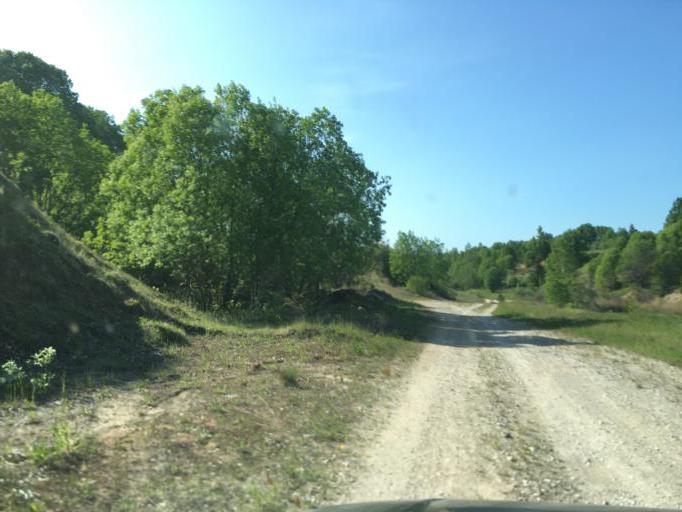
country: LV
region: Dundaga
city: Dundaga
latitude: 57.6108
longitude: 22.4412
